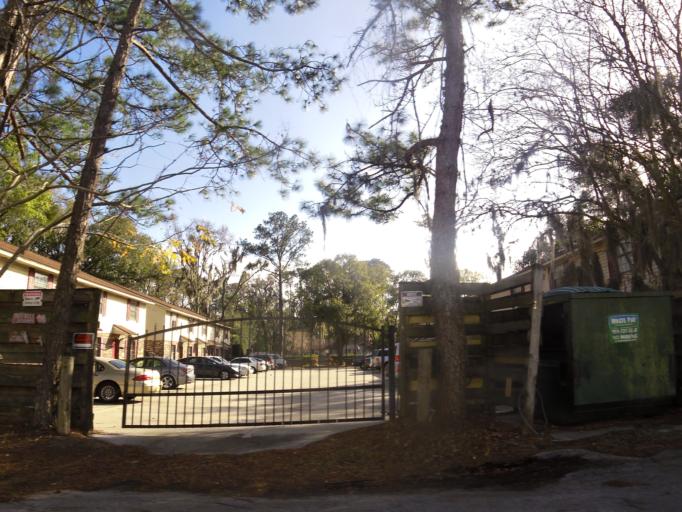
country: US
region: Florida
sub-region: Duval County
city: Jacksonville
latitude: 30.3009
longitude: -81.6291
